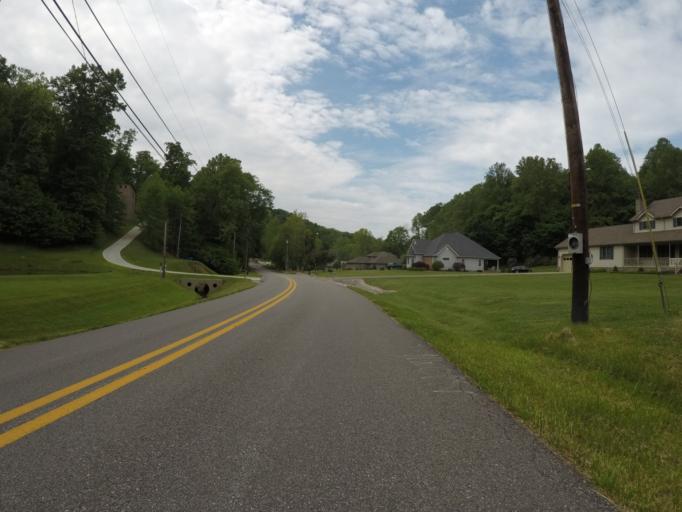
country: US
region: West Virginia
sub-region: Wayne County
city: Ceredo
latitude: 38.3516
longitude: -82.5624
